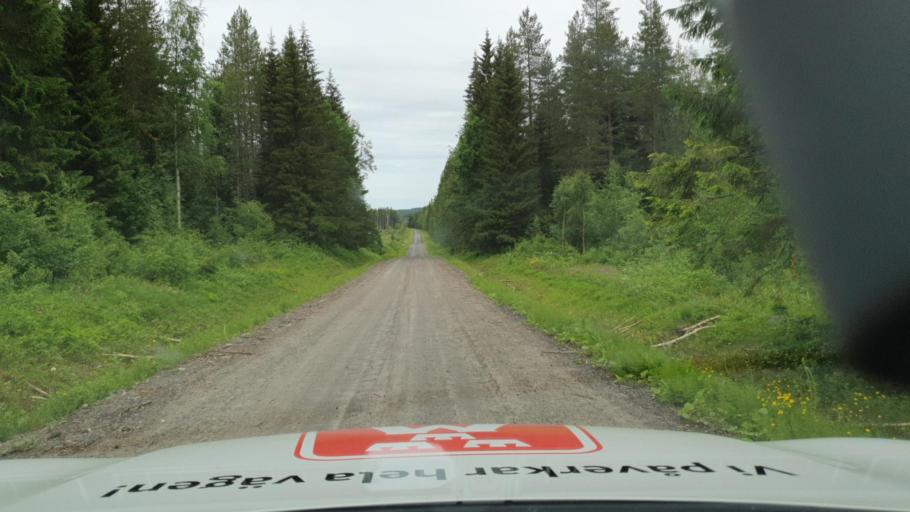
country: SE
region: Vaesterbotten
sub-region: Skelleftea Kommun
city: Burtraesk
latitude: 64.3781
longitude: 20.6150
